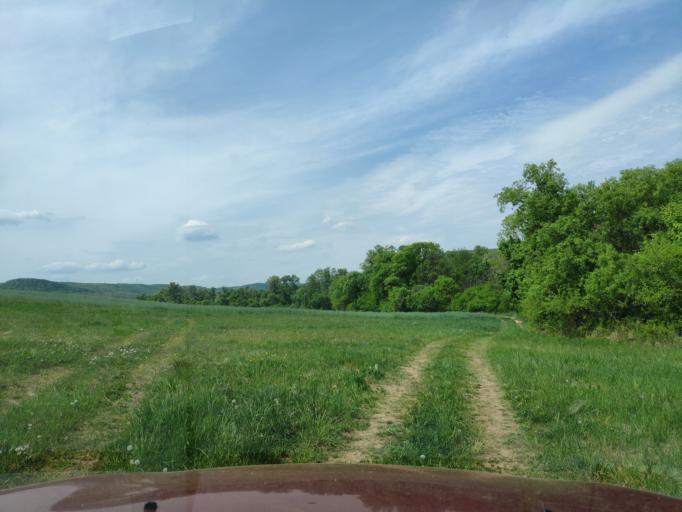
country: SK
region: Banskobystricky
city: Rimavska Sobota
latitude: 48.4773
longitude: 20.0810
